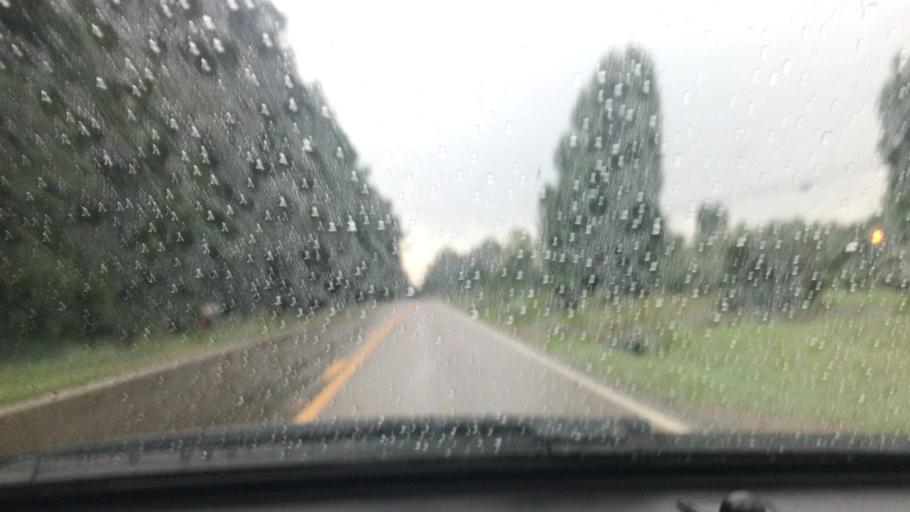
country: US
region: Mississippi
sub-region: Pike County
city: Summit
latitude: 31.2971
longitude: -90.5048
